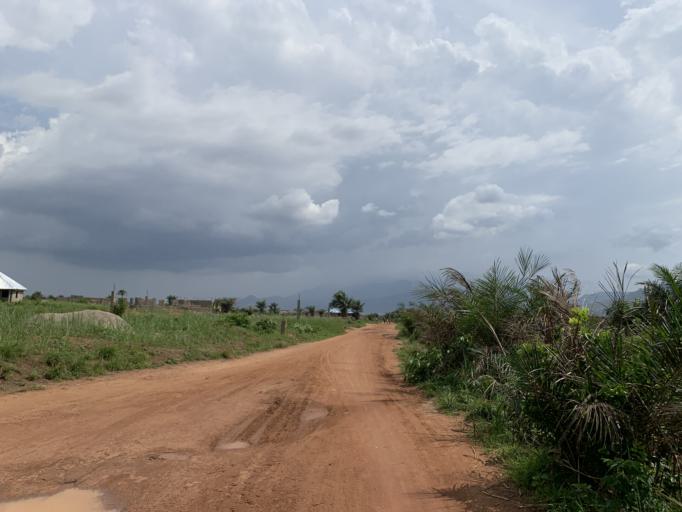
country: SL
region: Western Area
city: Waterloo
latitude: 8.3593
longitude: -13.0462
